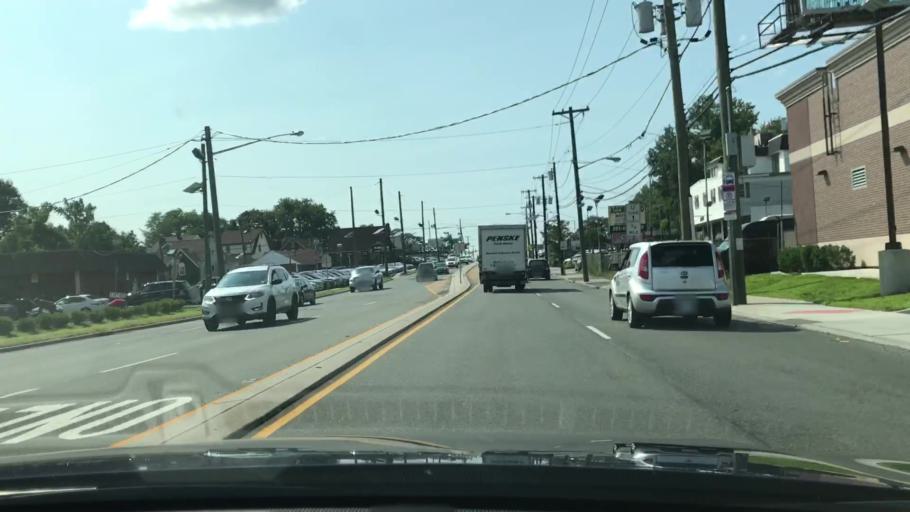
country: US
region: New Jersey
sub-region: Bergen County
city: Little Ferry
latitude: 40.8535
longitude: -74.0387
